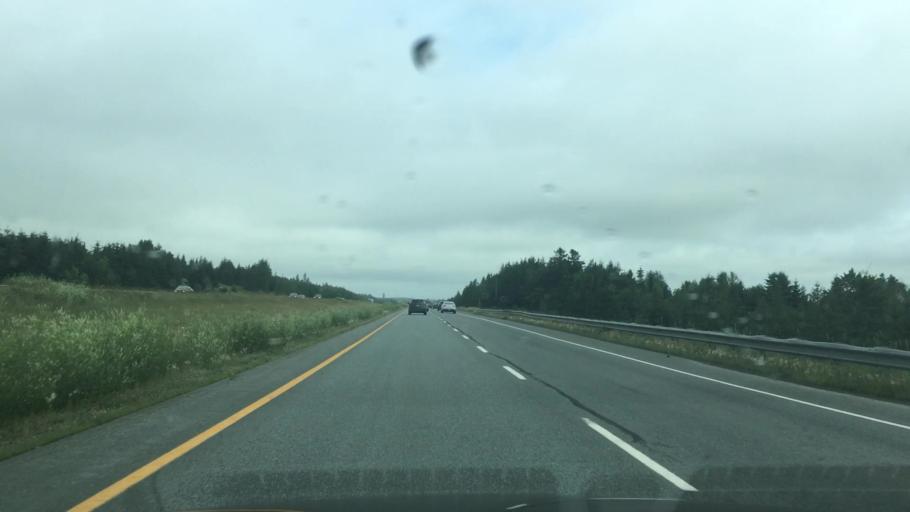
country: CA
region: Nova Scotia
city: Truro
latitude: 45.2843
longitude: -63.2977
